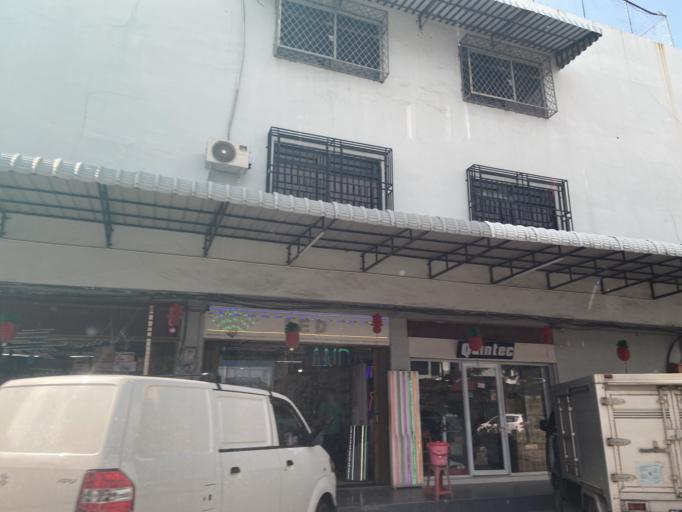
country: SG
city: Singapore
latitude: 1.1477
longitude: 104.0072
